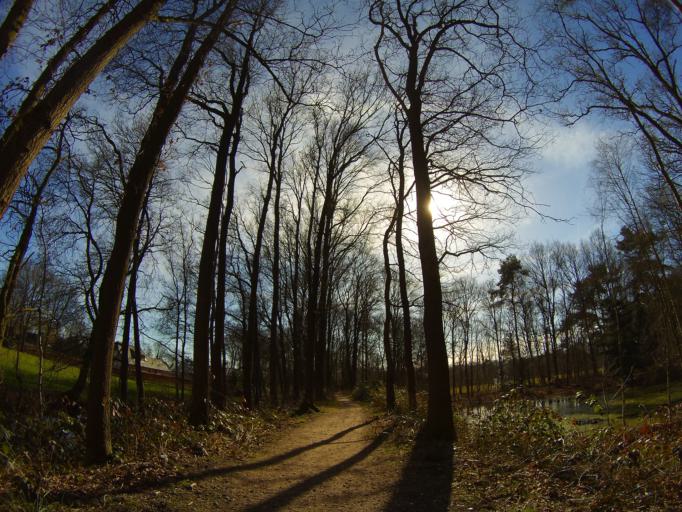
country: NL
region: Utrecht
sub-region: Gemeente Utrechtse Heuvelrug
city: Overberg
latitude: 52.0779
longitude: 5.5242
